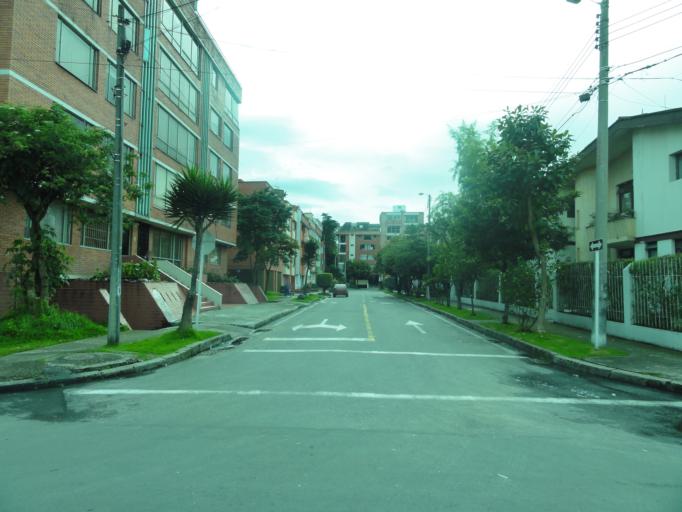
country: CO
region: Bogota D.C.
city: Bogota
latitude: 4.6455
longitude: -74.0819
